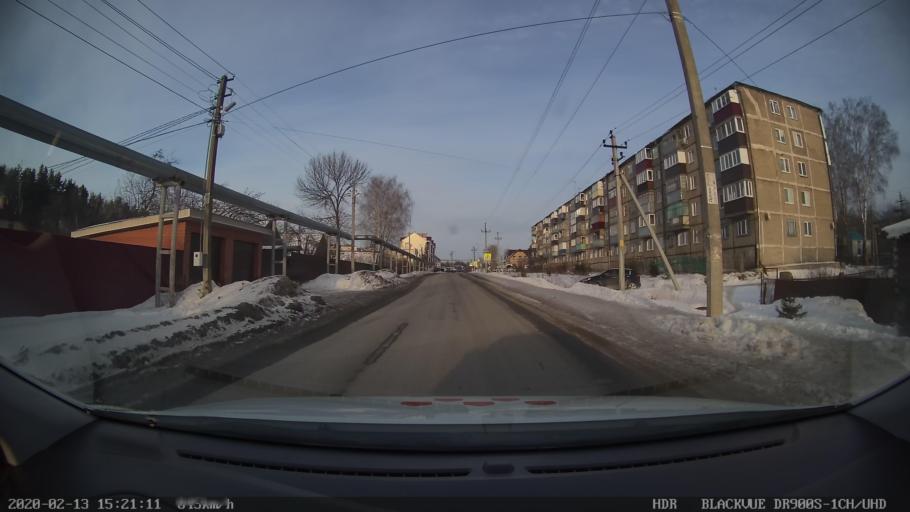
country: RU
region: Tatarstan
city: Vysokaya Gora
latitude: 55.9179
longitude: 49.2992
